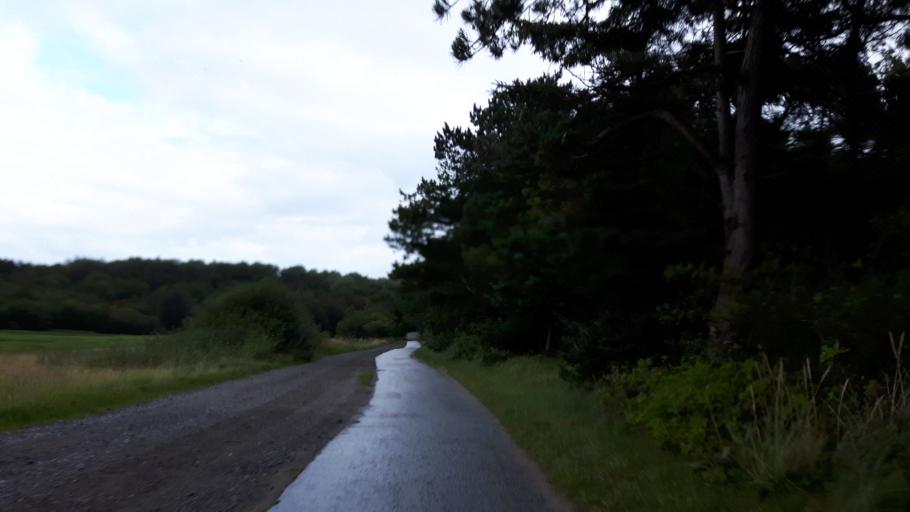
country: NL
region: Friesland
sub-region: Gemeente Ameland
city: Nes
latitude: 53.4513
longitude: 5.7571
